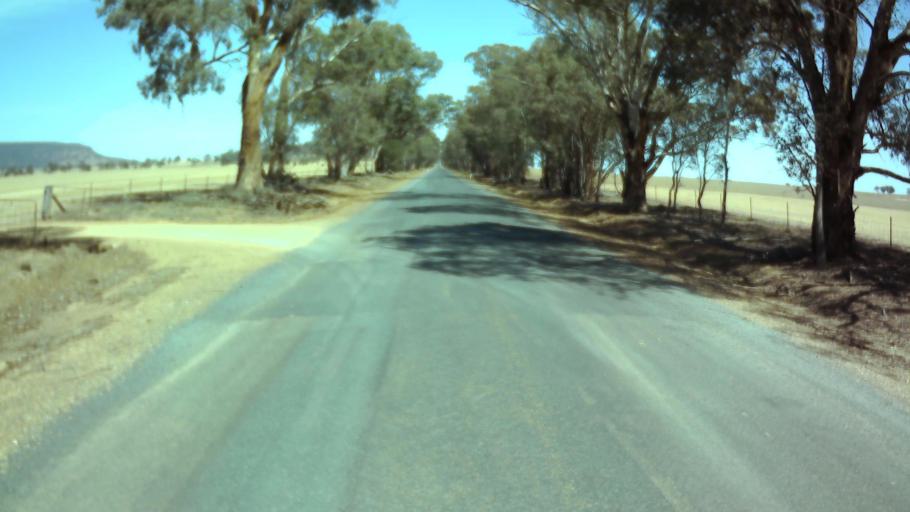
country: AU
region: New South Wales
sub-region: Weddin
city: Grenfell
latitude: -33.8638
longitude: 148.0351
